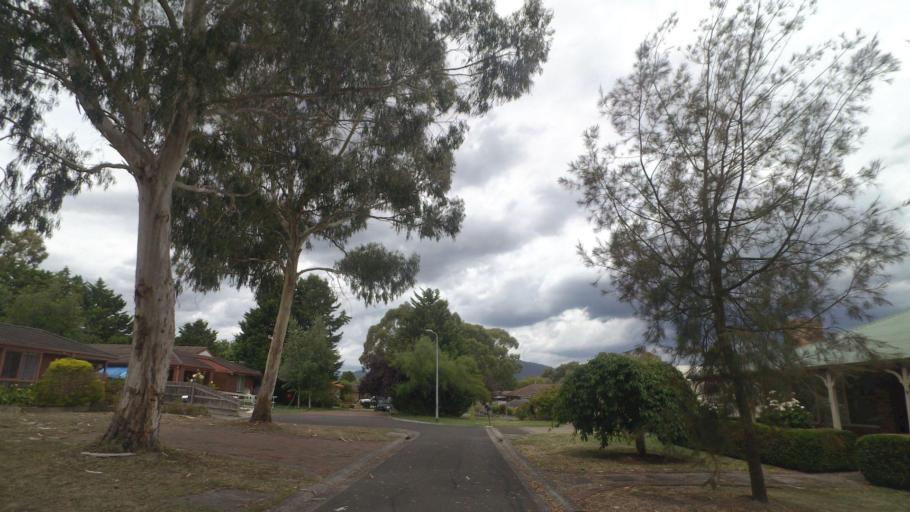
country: AU
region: Victoria
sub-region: Maroondah
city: Bayswater North
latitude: -37.8182
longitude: 145.2837
